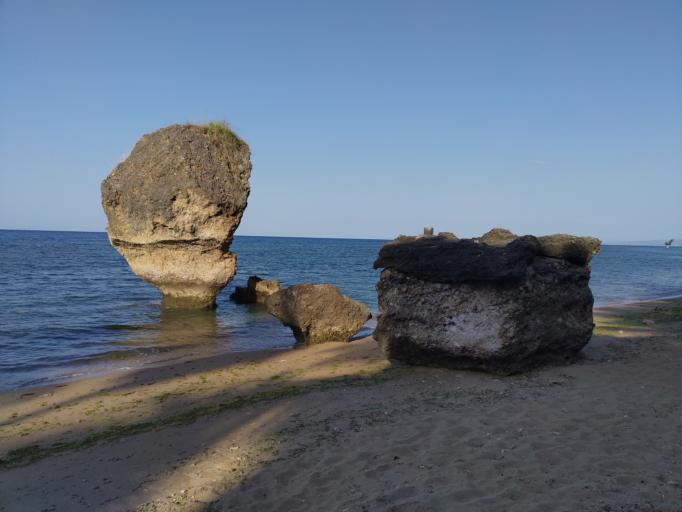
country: TL
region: Baucau
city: Baucau
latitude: -8.4441
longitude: 126.4760
